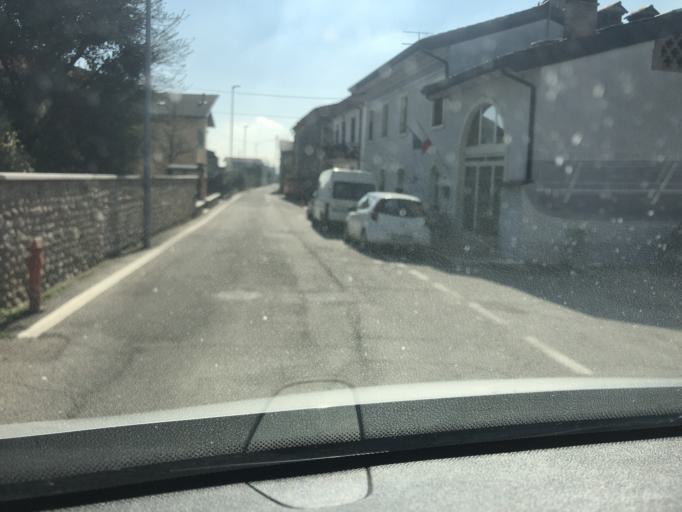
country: IT
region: Veneto
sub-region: Provincia di Verona
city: Villafranca di Verona
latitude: 45.3754
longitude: 10.8241
